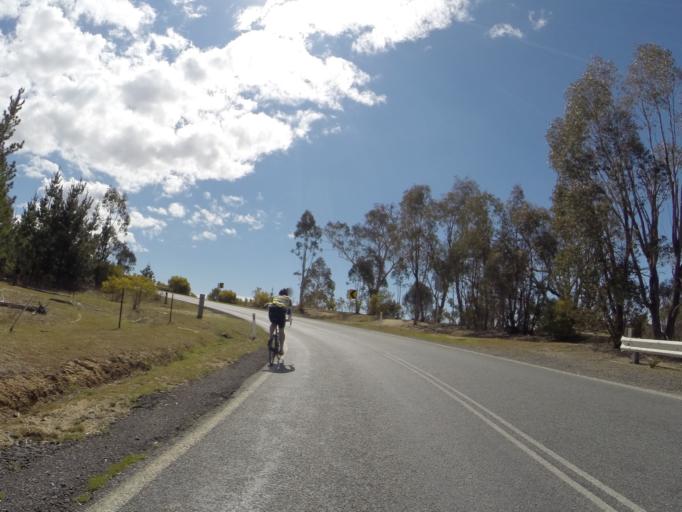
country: AU
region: Australian Capital Territory
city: Macquarie
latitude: -35.3611
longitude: 148.9509
